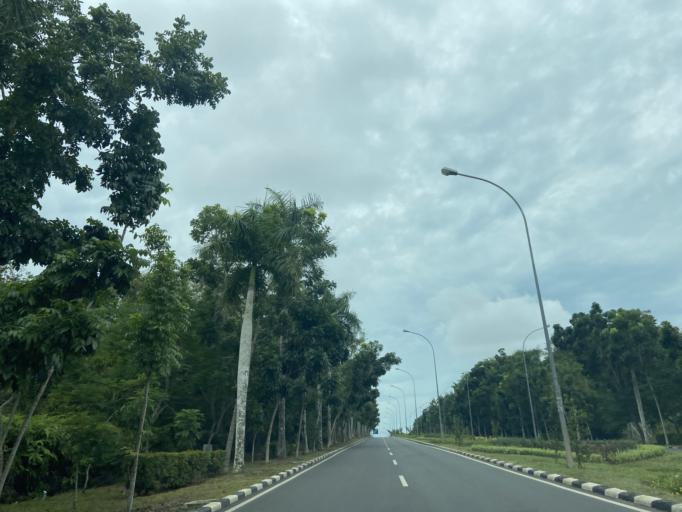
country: SG
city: Singapore
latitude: 1.1260
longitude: 104.1095
